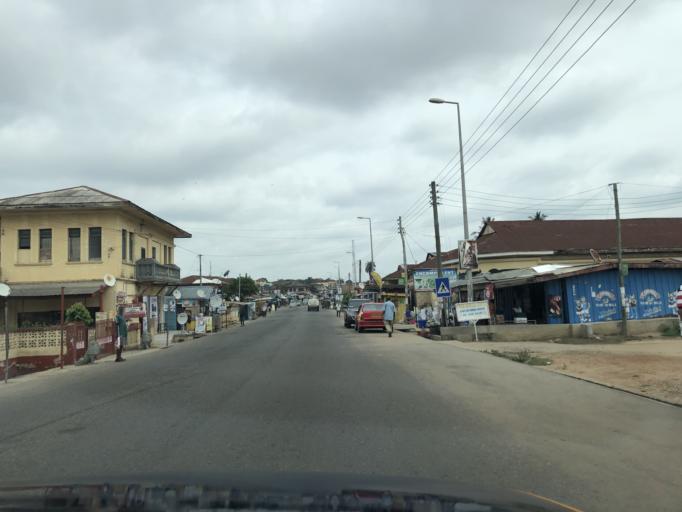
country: GH
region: Eastern
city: Koforidua
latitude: 6.0966
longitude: -0.2616
